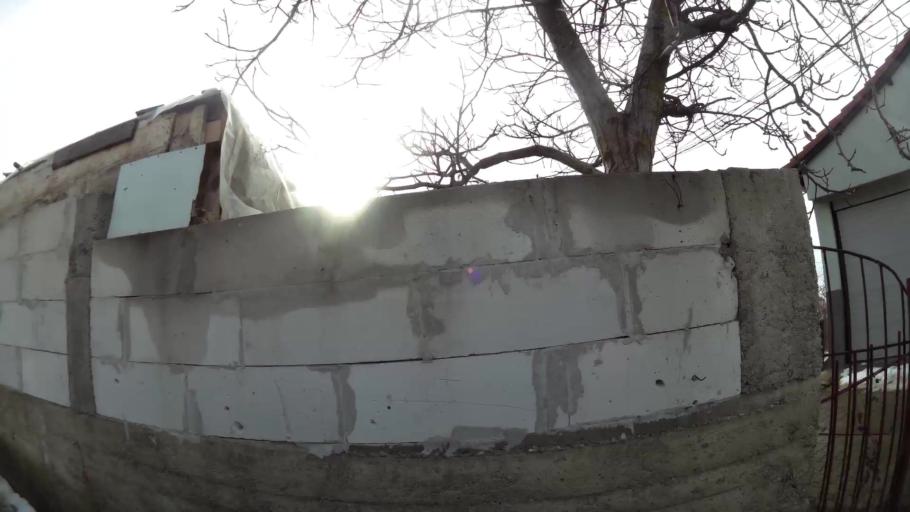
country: XK
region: Pristina
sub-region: Komuna e Prishtines
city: Pristina
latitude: 42.6705
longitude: 21.1877
